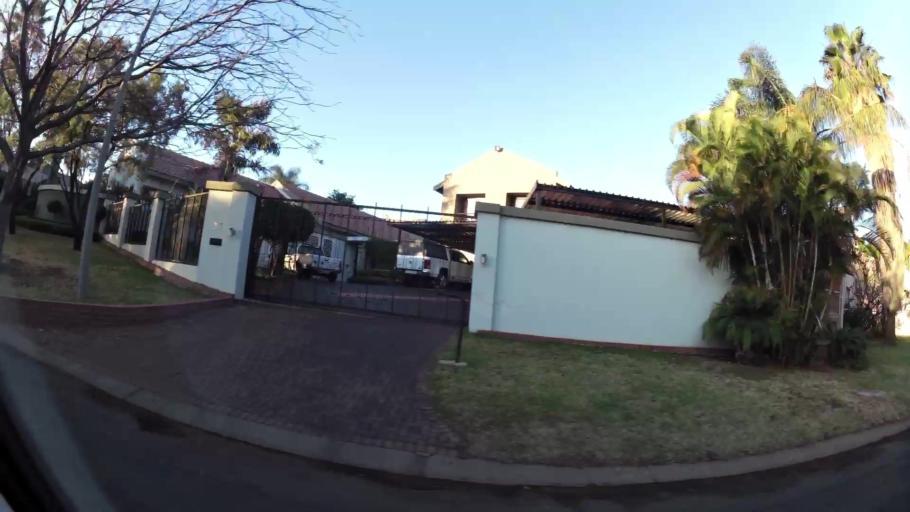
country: ZA
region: North-West
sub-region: Bojanala Platinum District Municipality
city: Rustenburg
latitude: -25.6999
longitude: 27.2394
